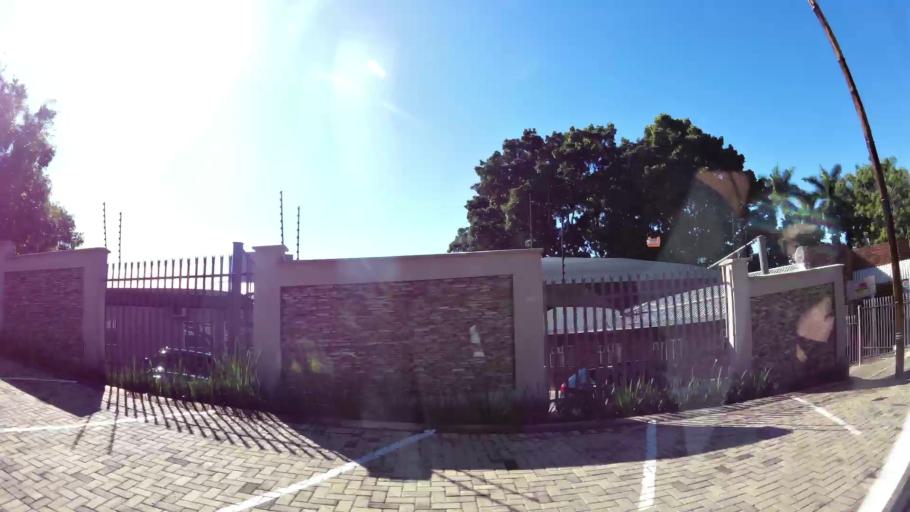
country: ZA
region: Limpopo
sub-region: Mopani District Municipality
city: Tzaneen
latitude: -23.8341
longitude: 30.1560
